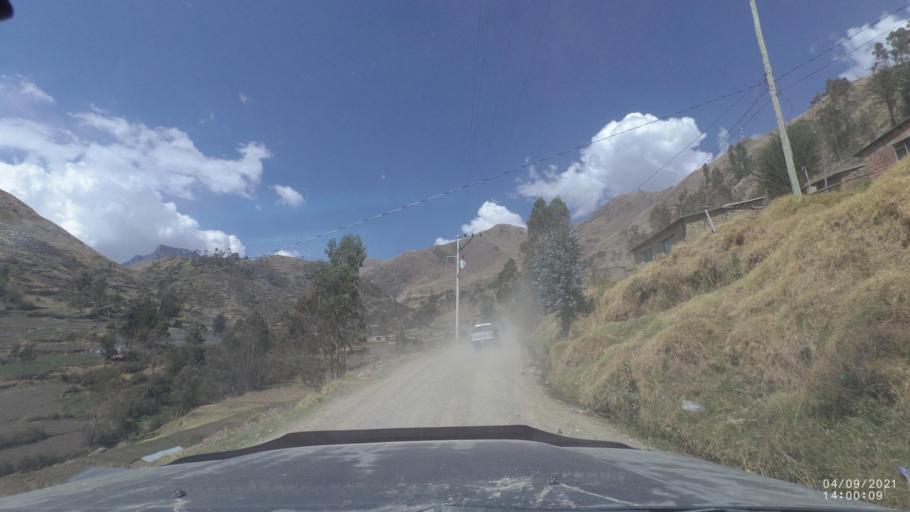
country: BO
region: Cochabamba
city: Sipe Sipe
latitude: -17.2316
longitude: -66.4856
